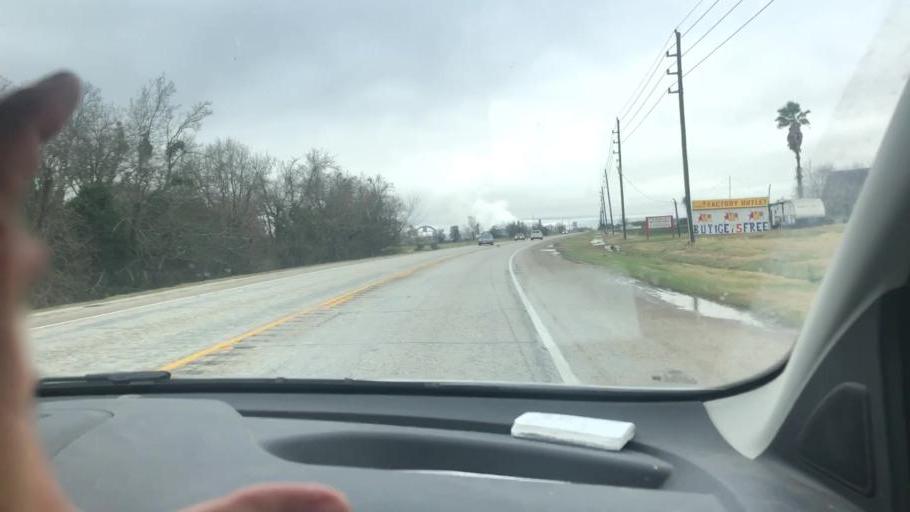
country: US
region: Texas
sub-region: Wharton County
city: Wharton
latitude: 29.3038
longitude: -96.0804
